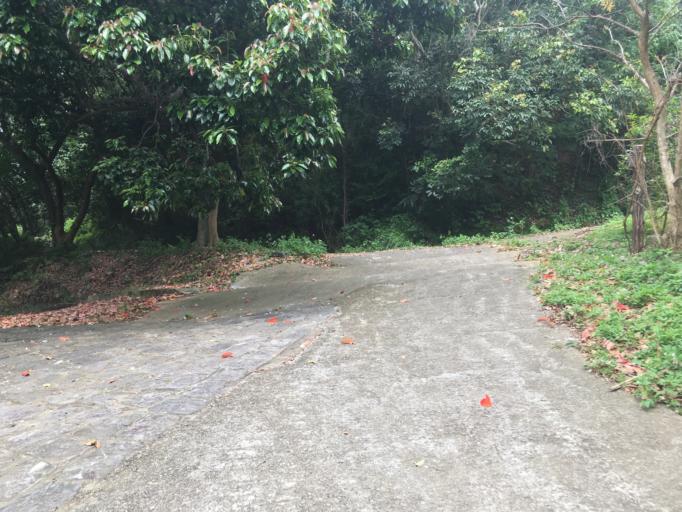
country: TW
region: Taiwan
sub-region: Hsinchu
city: Hsinchu
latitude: 24.7420
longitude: 120.9787
